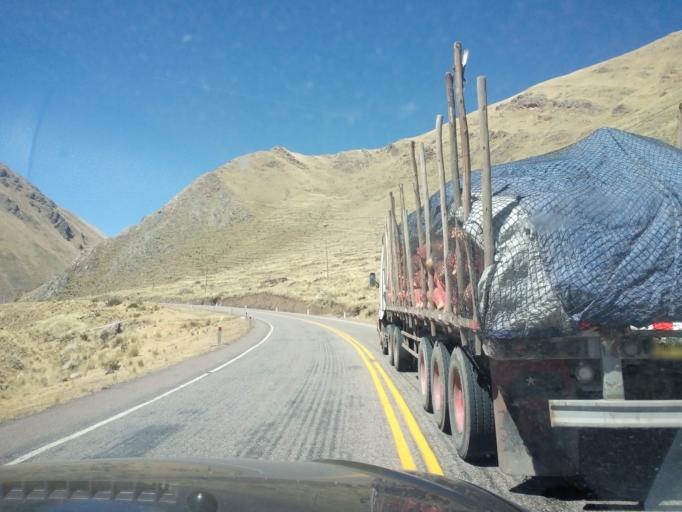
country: PE
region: Cusco
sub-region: Provincia de Canas
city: Layo
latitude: -14.4491
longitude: -71.0812
